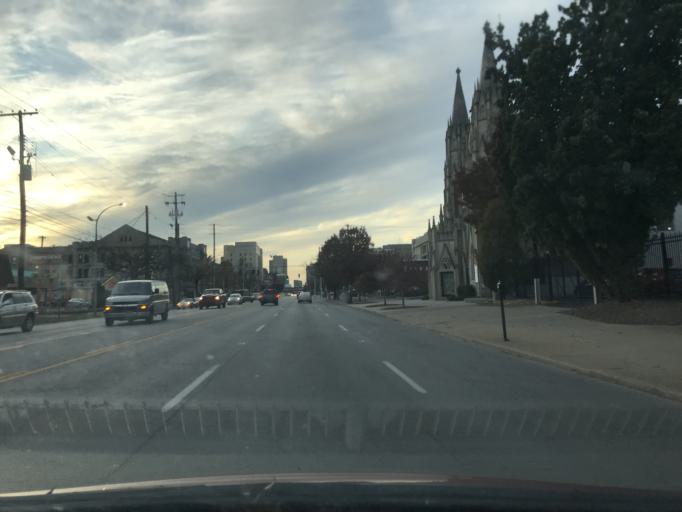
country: US
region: Kentucky
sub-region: Jefferson County
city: Louisville
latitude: 38.2452
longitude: -85.7462
